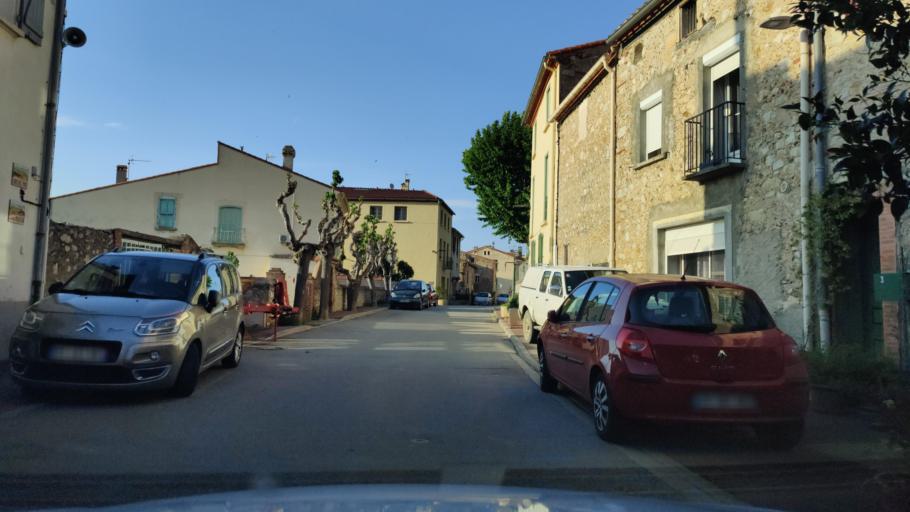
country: FR
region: Languedoc-Roussillon
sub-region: Departement des Pyrenees-Orientales
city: Estagel
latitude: 42.8129
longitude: 2.7447
